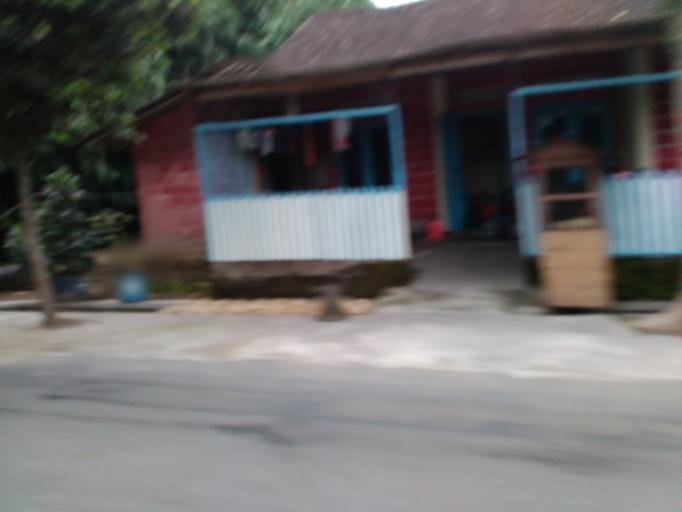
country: ID
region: Central Java
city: Boyolali
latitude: -7.5235
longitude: 110.5945
